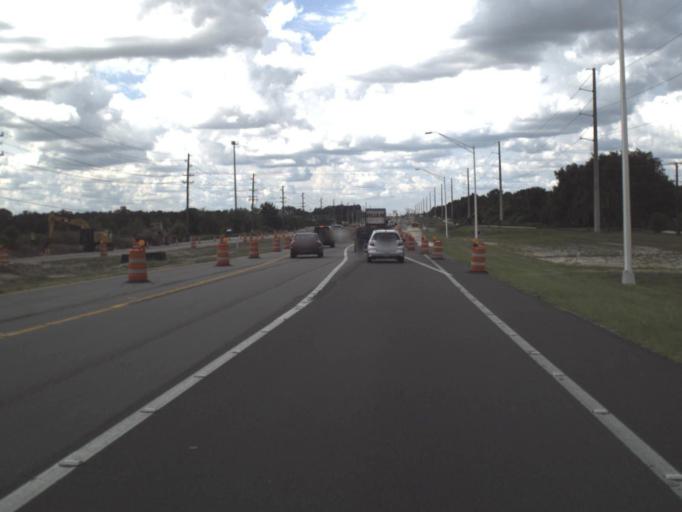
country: US
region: Florida
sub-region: Polk County
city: Highland City
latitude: 27.9816
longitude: -81.8890
